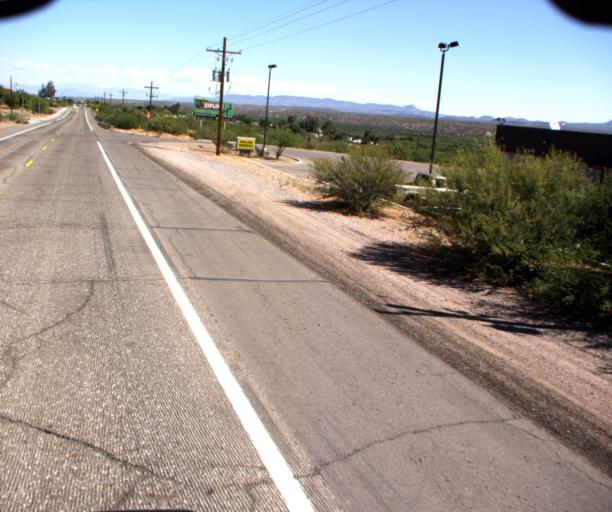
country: US
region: Arizona
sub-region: Pinal County
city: Mammoth
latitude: 32.7253
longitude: -110.6456
